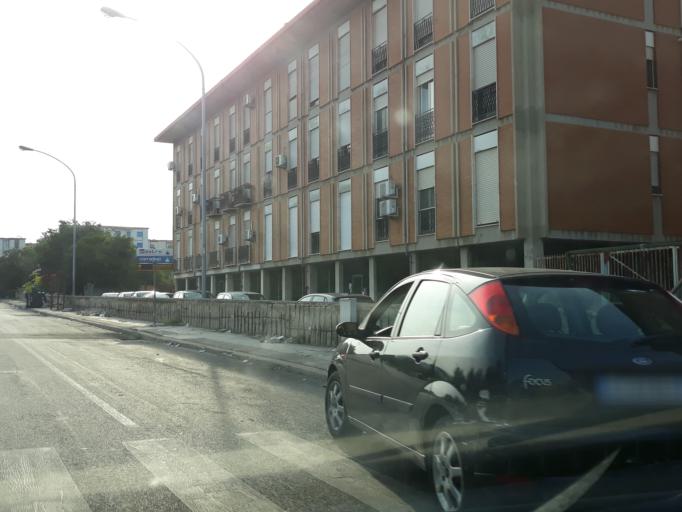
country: IT
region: Sicily
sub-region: Palermo
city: Ciaculli
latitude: 38.0888
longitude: 13.3604
